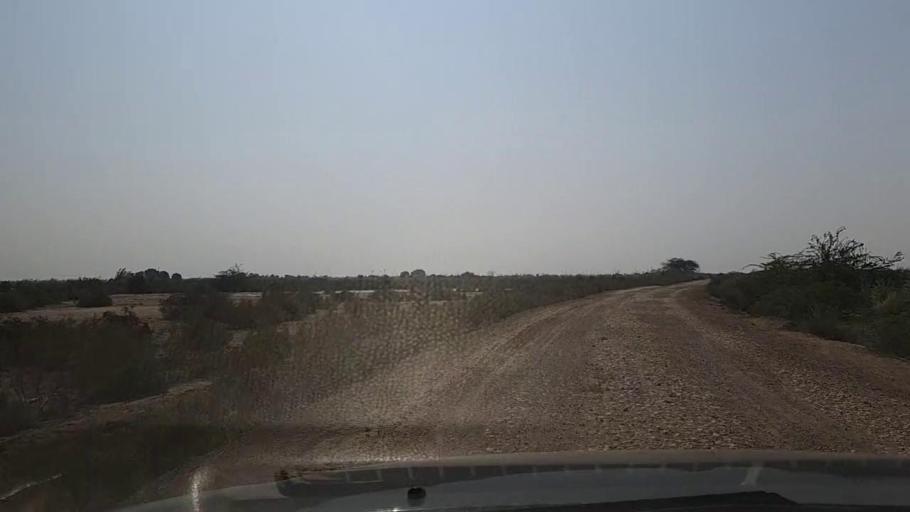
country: PK
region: Sindh
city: Mirpur Sakro
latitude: 24.3811
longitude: 67.6610
